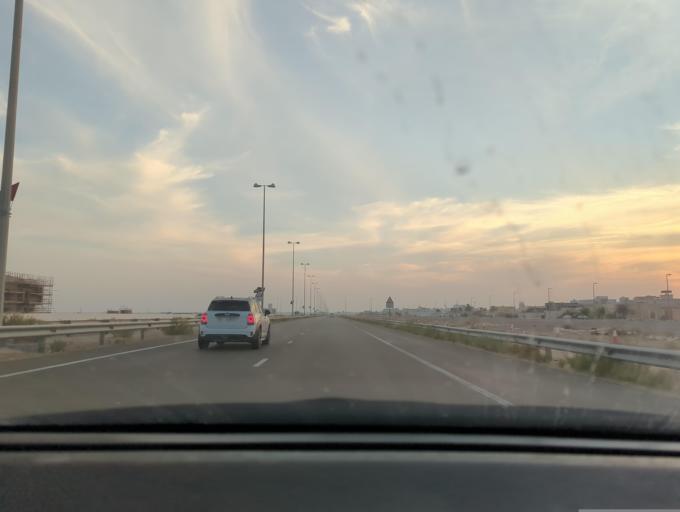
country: AE
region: Abu Dhabi
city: Abu Dhabi
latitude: 24.3513
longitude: 54.6616
